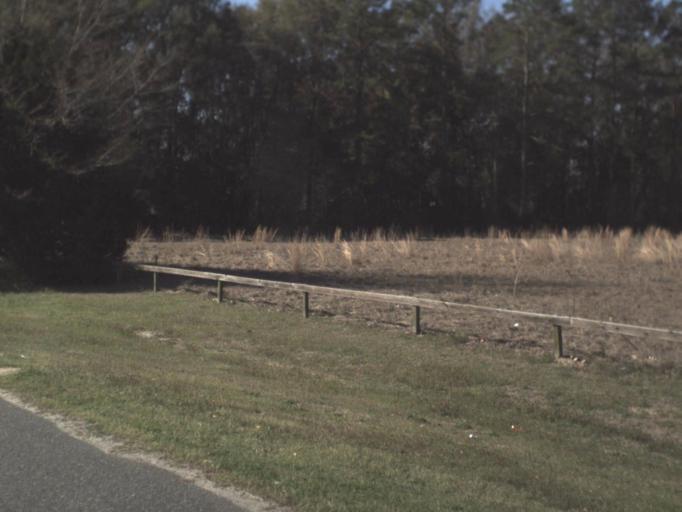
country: US
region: Florida
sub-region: Jackson County
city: Malone
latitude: 30.8824
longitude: -85.1614
